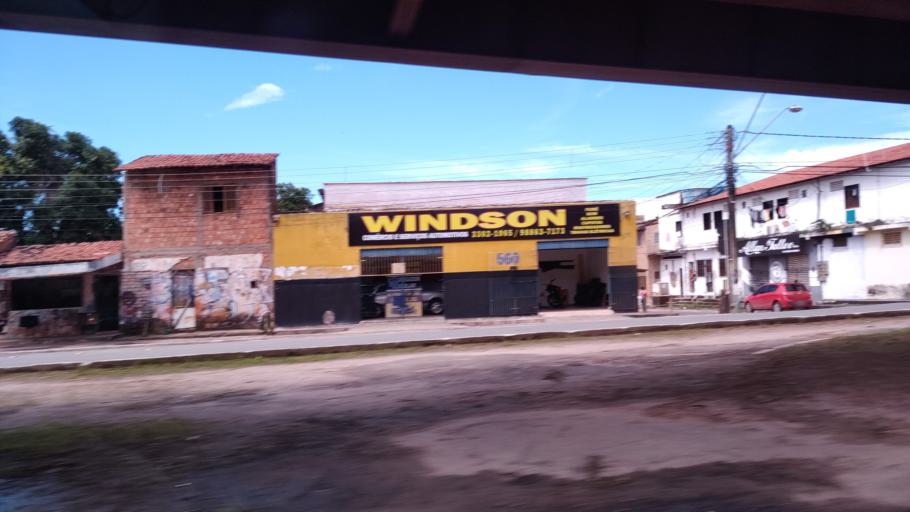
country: BR
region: Maranhao
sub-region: Sao Luis
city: Sao Luis
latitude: -2.5377
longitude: -44.2721
